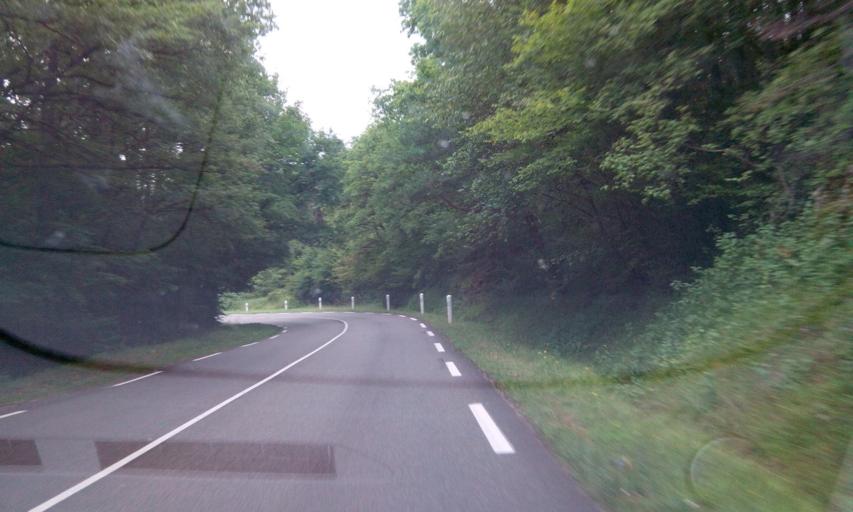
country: FR
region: Limousin
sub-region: Departement de la Correze
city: Cosnac
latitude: 45.0663
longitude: 1.5629
